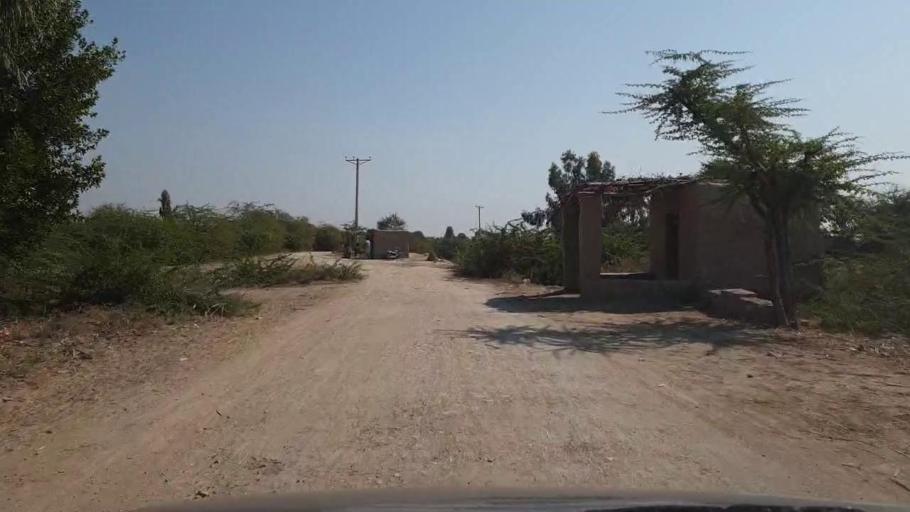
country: PK
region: Sindh
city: Samaro
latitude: 25.2550
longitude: 69.2643
